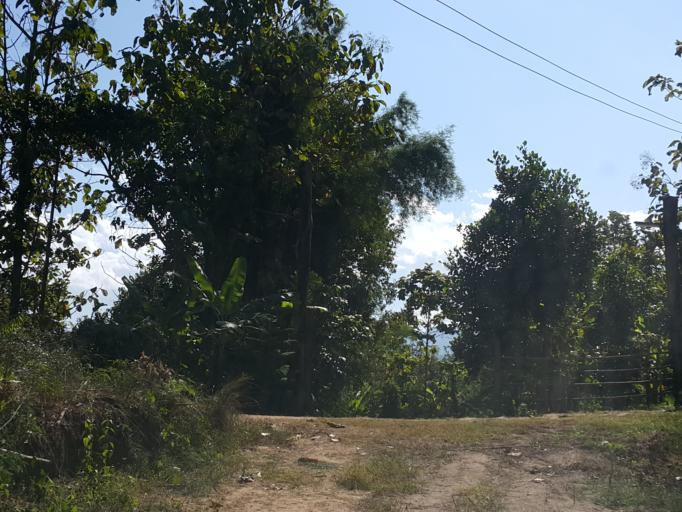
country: TH
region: Chiang Mai
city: Mae Taeng
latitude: 18.9554
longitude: 98.9008
